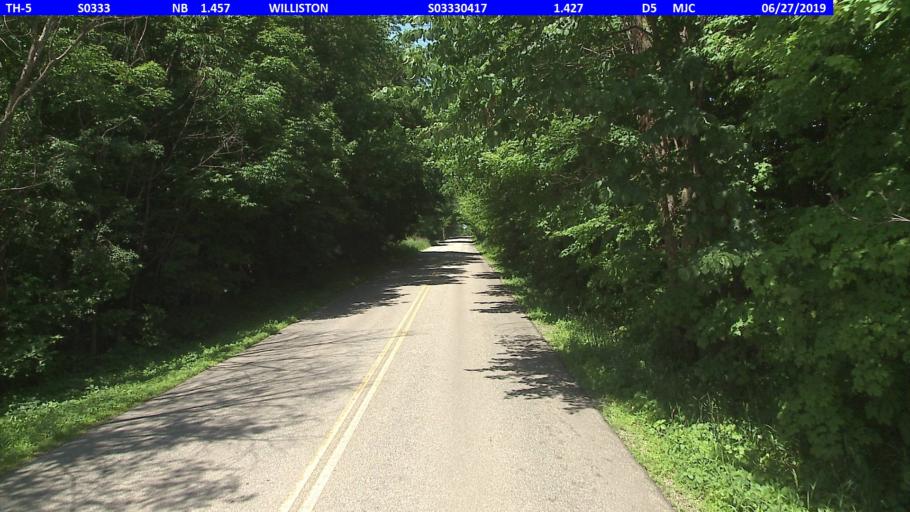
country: US
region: Vermont
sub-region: Chittenden County
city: South Burlington
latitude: 44.4217
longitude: -73.1356
